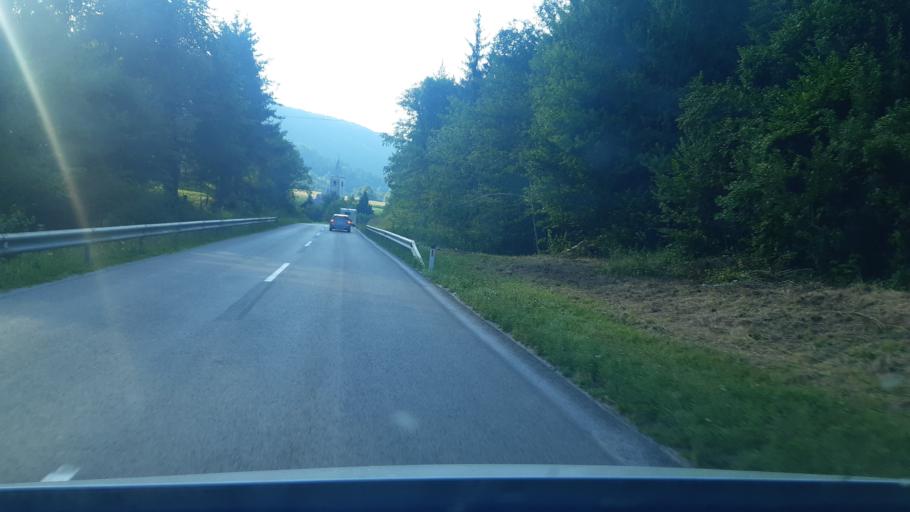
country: SI
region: Semic
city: Semic
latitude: 45.6637
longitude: 15.1109
